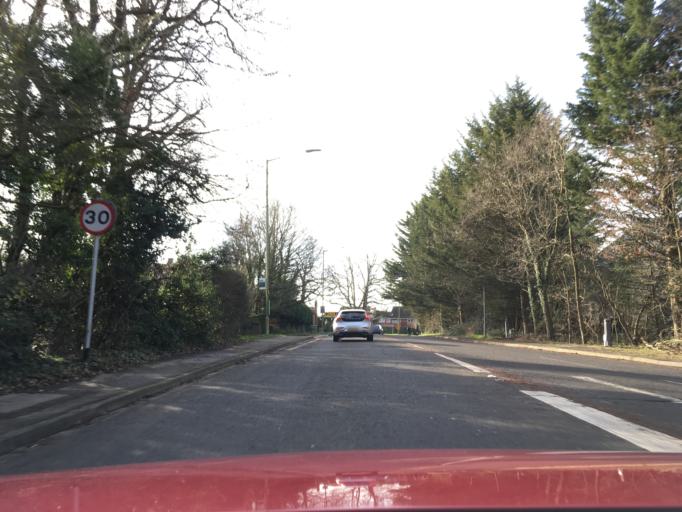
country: GB
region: England
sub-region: West Berkshire
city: Tilehurst
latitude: 51.4426
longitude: -1.0326
